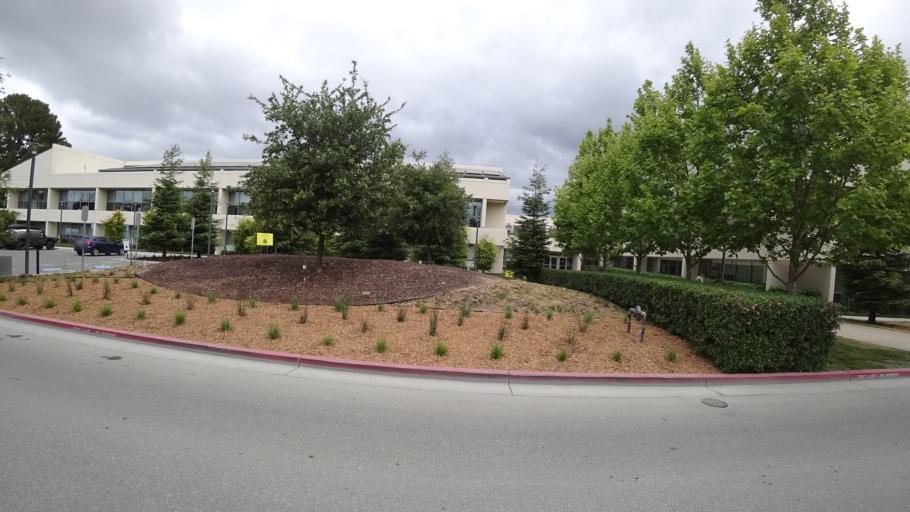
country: US
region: California
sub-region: Santa Clara County
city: Los Altos Hills
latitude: 37.3988
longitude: -122.1387
